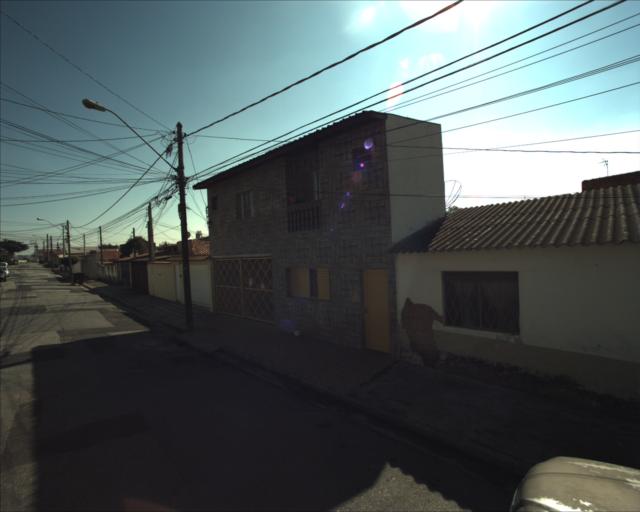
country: BR
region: Sao Paulo
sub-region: Sorocaba
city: Sorocaba
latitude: -23.5033
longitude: -47.4415
